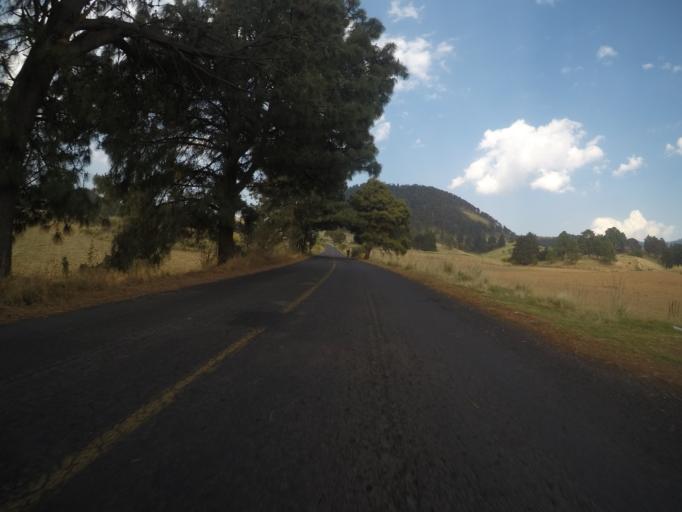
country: MX
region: Mexico
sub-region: Xalatlaco
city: San Juan Tomasquillo Herradura
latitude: 19.1624
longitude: -99.3887
